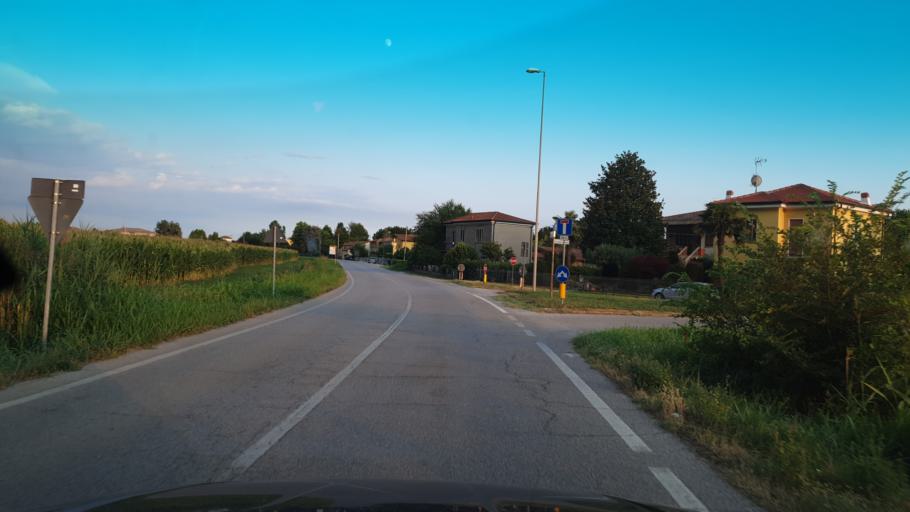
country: IT
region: Veneto
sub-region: Provincia di Rovigo
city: Lendinara
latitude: 45.0760
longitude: 11.6116
